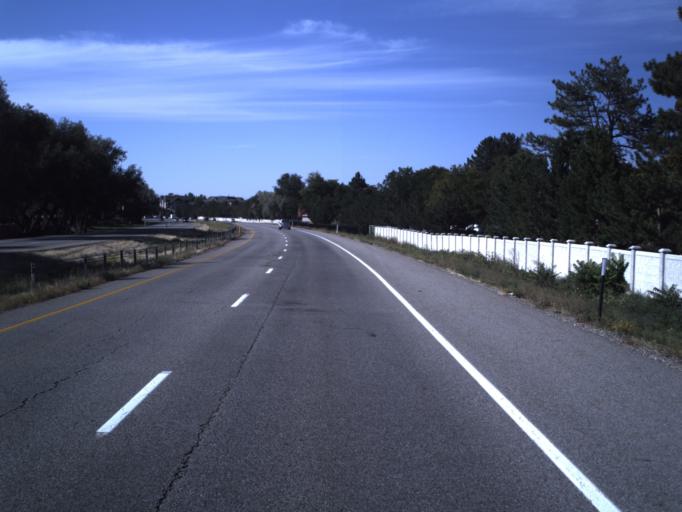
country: US
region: Utah
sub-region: Salt Lake County
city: Holladay
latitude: 40.6543
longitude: -111.8507
